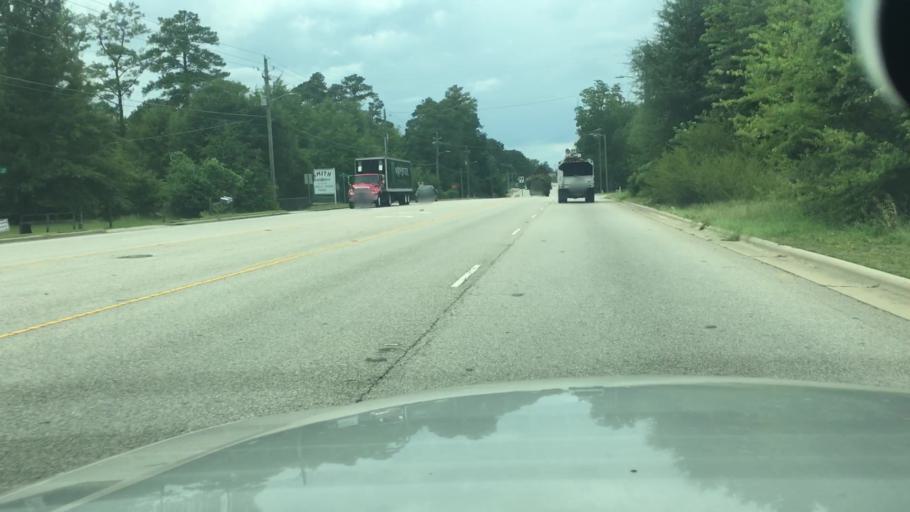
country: US
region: North Carolina
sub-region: Cumberland County
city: Fayetteville
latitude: 34.9983
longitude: -78.8948
